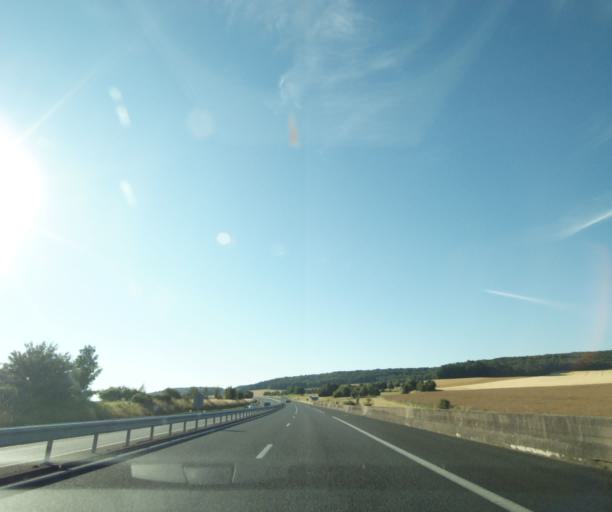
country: FR
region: Bourgogne
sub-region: Departement de l'Yonne
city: Soucy
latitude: 48.2491
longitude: 3.3434
